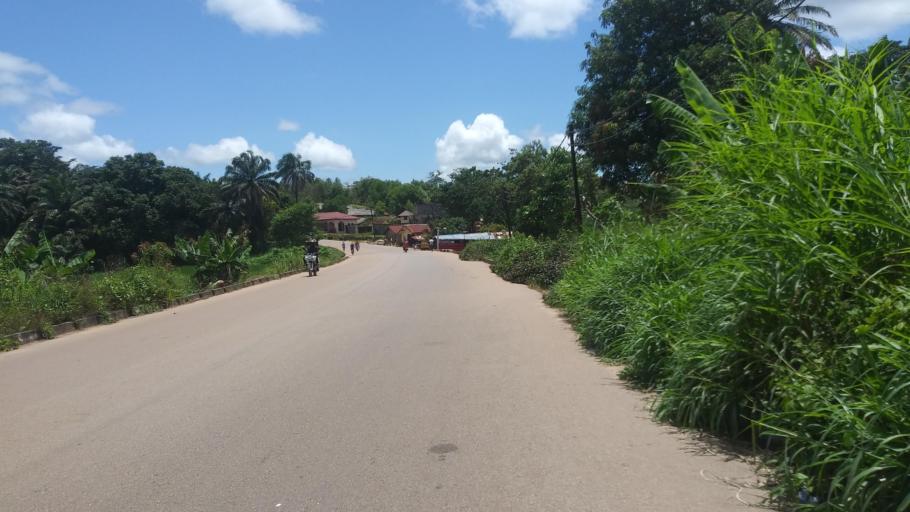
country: SL
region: Northern Province
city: Makeni
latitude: 8.8792
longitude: -12.0290
